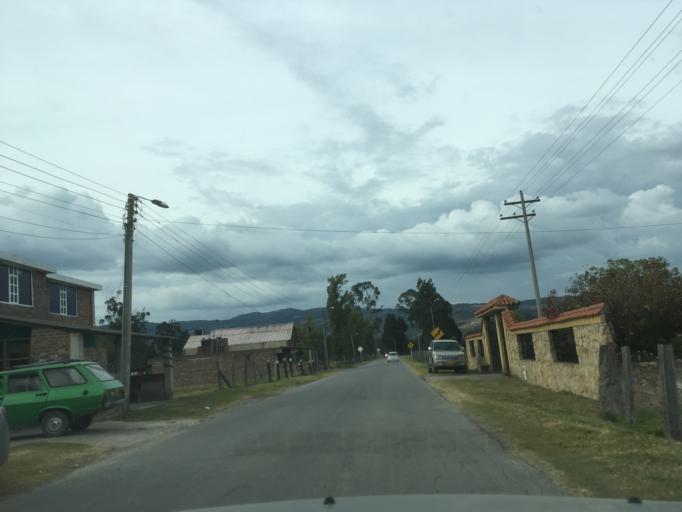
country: CO
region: Boyaca
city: Firavitoba
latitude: 5.6581
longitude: -72.9904
